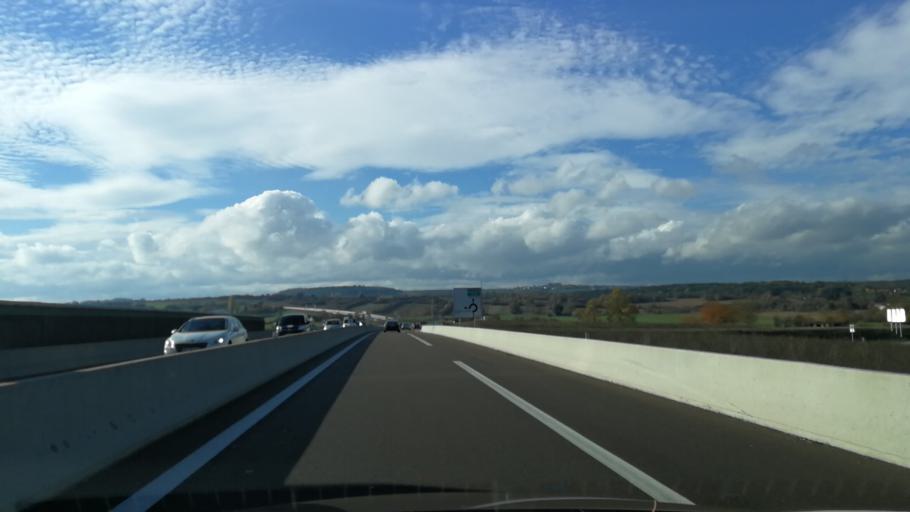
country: FR
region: Bourgogne
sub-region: Departement de la Cote-d'Or
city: Ahuy
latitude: 47.3585
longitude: 5.0352
